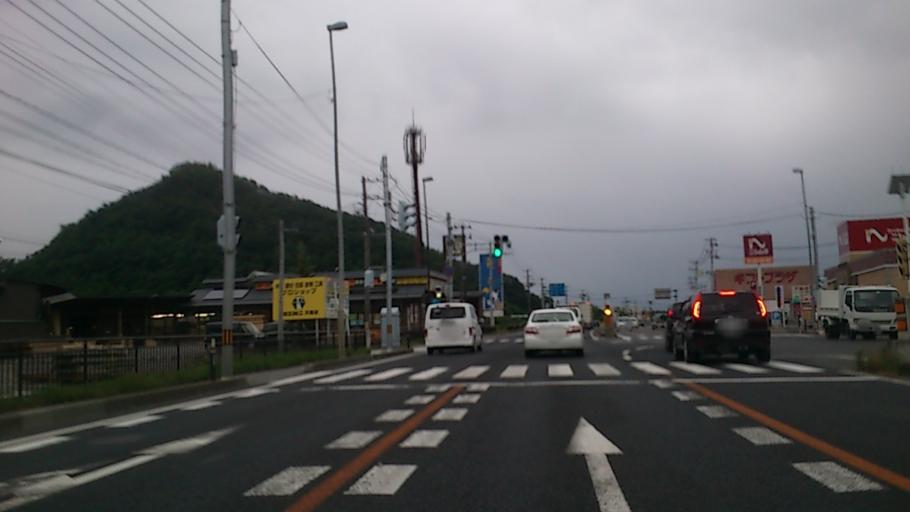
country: JP
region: Yamagata
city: Tendo
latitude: 38.3531
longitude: 140.3875
